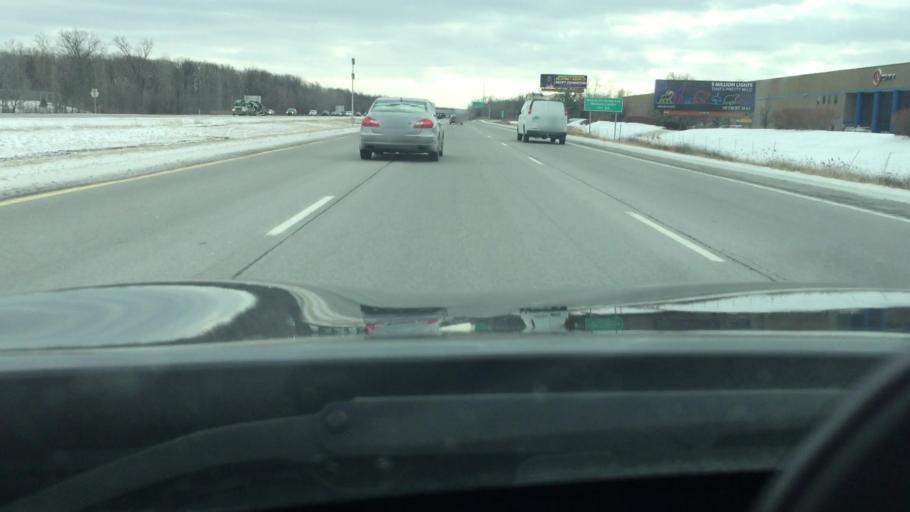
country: US
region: Michigan
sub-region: Wayne County
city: Romulus
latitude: 42.2585
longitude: -83.4407
